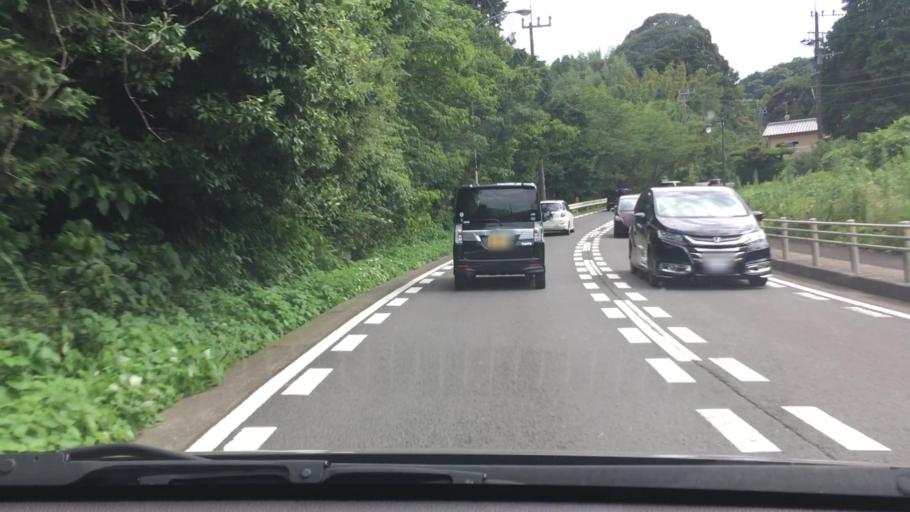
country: JP
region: Nagasaki
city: Togitsu
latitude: 32.9317
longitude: 129.7833
